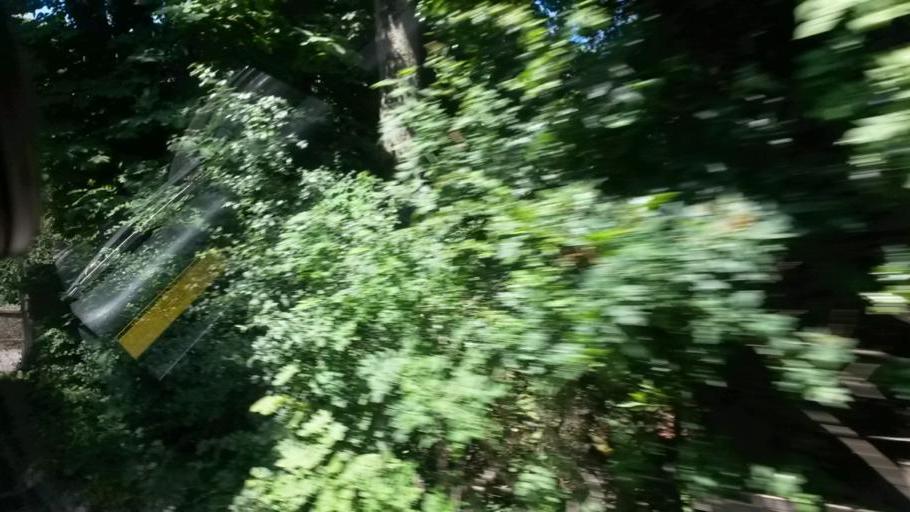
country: IE
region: Leinster
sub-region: Fingal County
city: Swords
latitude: 53.5157
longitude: -6.2446
